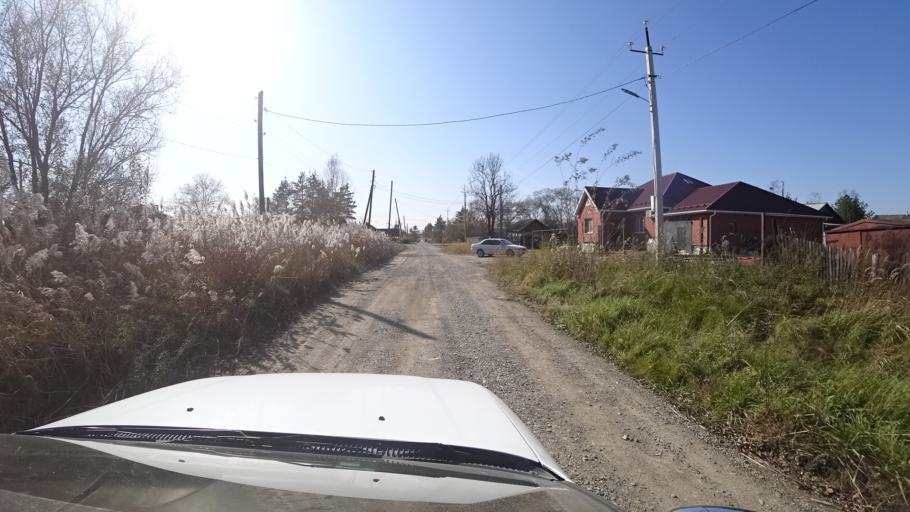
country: RU
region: Primorskiy
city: Dal'nerechensk
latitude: 45.9264
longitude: 133.7389
